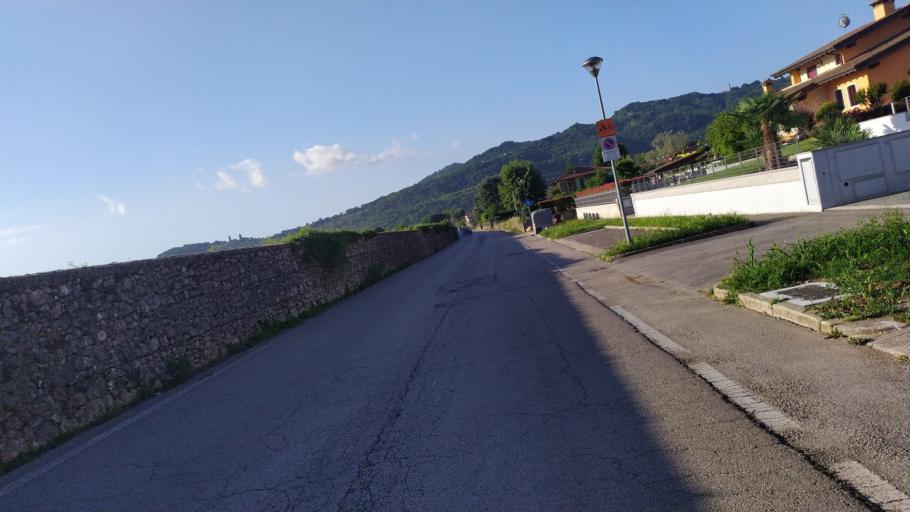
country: IT
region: Veneto
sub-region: Provincia di Vicenza
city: Malo
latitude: 45.6364
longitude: 11.4226
